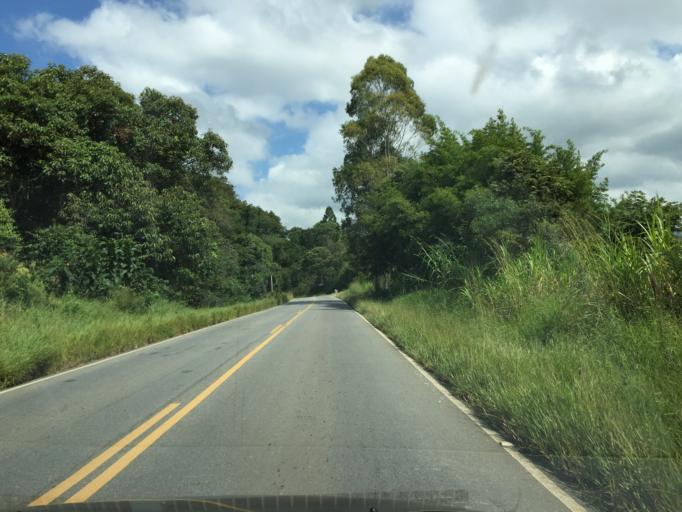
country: BR
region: Minas Gerais
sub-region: Passa Quatro
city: Passa Quatro
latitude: -22.3776
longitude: -44.9642
